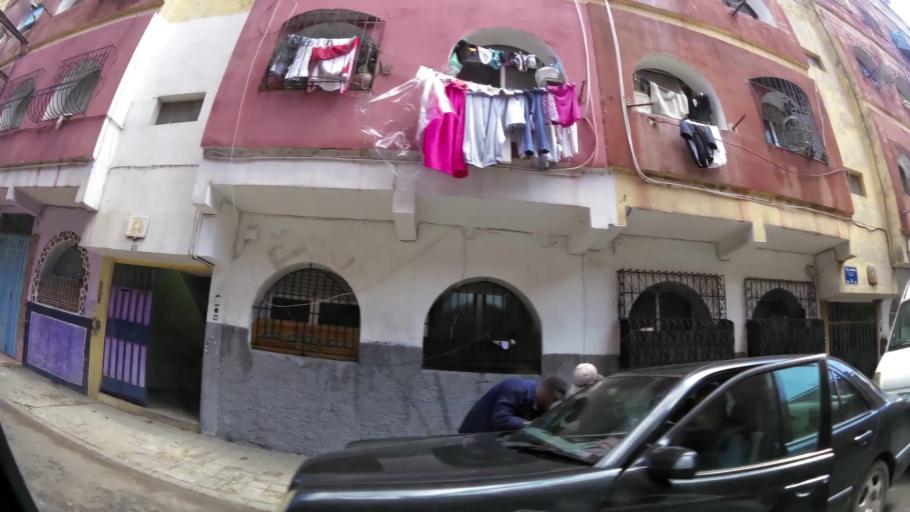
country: MA
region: Grand Casablanca
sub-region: Mediouna
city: Tit Mellil
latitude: 33.5369
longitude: -7.5516
